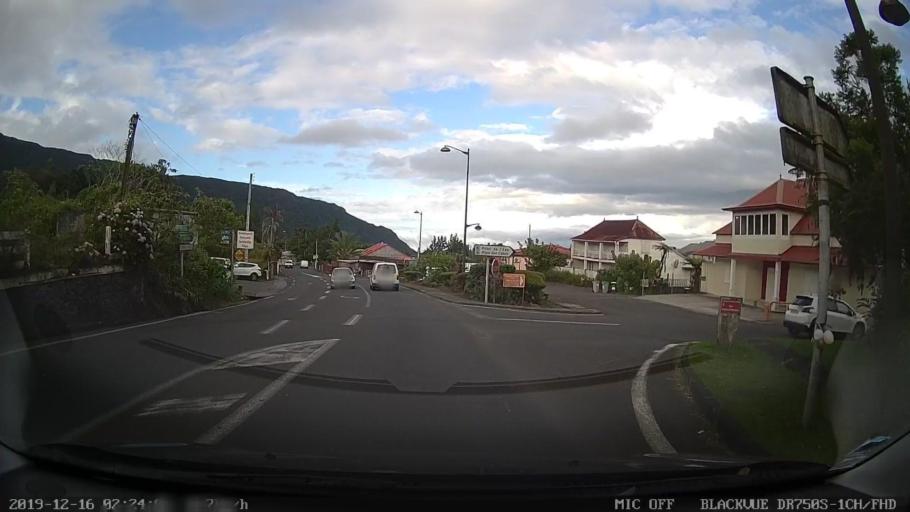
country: RE
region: Reunion
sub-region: Reunion
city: Salazie
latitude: -21.1402
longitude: 55.6227
